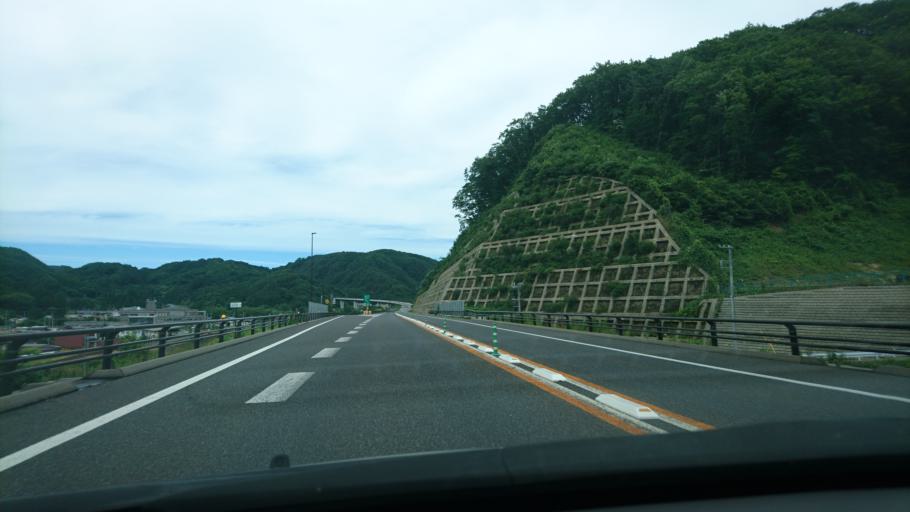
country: JP
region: Iwate
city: Miyako
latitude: 40.0005
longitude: 141.8862
